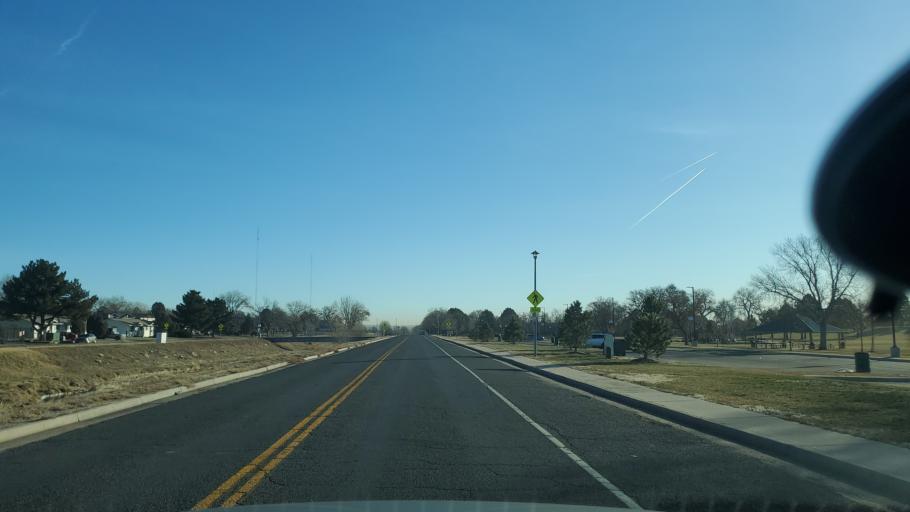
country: US
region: Colorado
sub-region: Adams County
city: Welby
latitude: 39.8419
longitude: -104.9666
